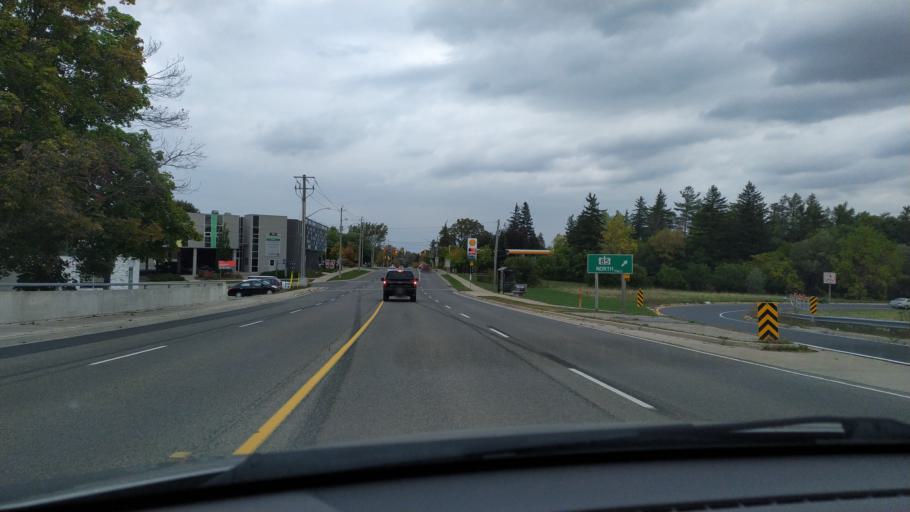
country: CA
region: Ontario
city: Waterloo
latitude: 43.4745
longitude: -80.4844
